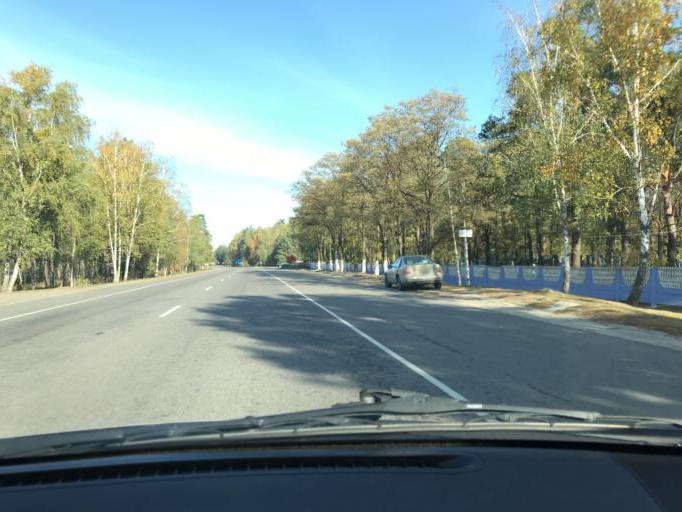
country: BY
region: Brest
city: Mikashevichy
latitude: 52.2356
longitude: 27.4486
